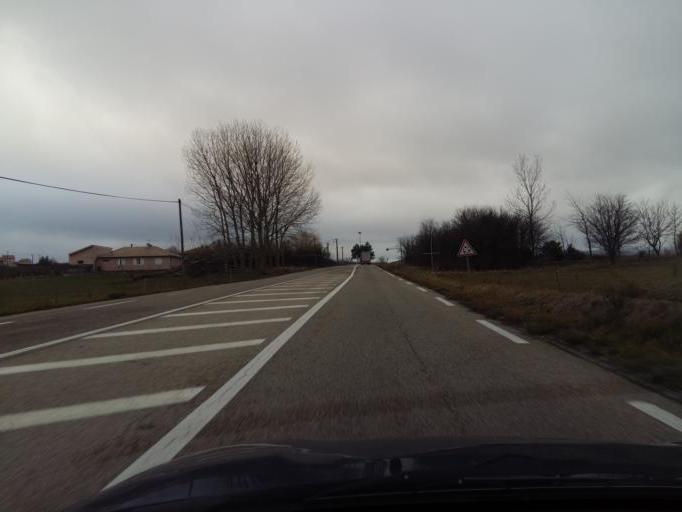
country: FR
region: Rhone-Alpes
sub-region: Departement de l'Ardeche
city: Saint-Cyr
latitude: 45.2480
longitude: 4.7455
